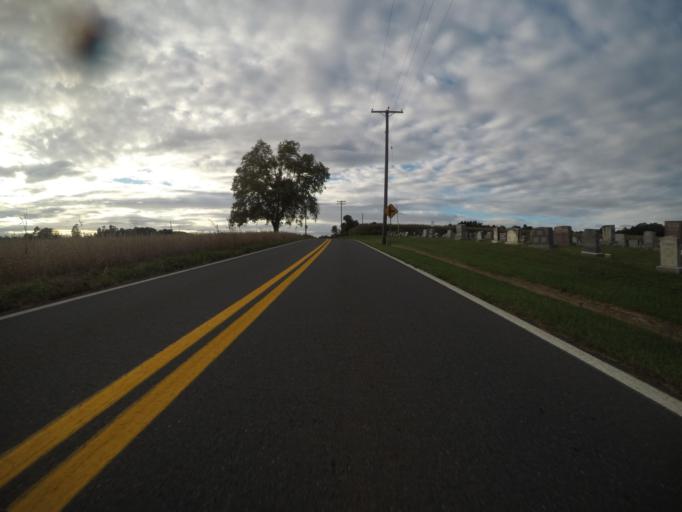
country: US
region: Maryland
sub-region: Carroll County
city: Hampstead
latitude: 39.5558
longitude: -76.8814
